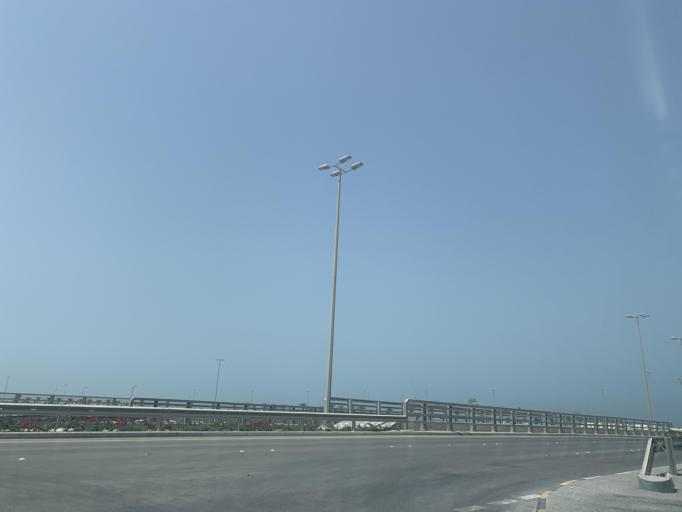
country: BH
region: Muharraq
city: Al Hadd
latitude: 26.2743
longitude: 50.6752
